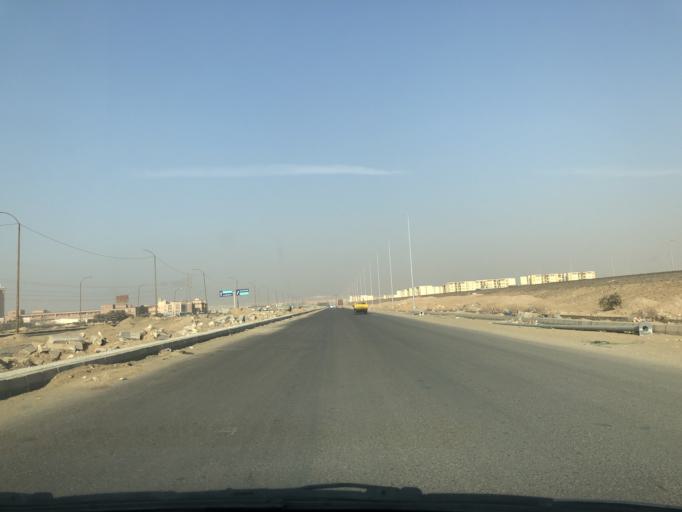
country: EG
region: Al Jizah
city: Madinat Sittah Uktubar
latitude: 29.9001
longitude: 30.9081
